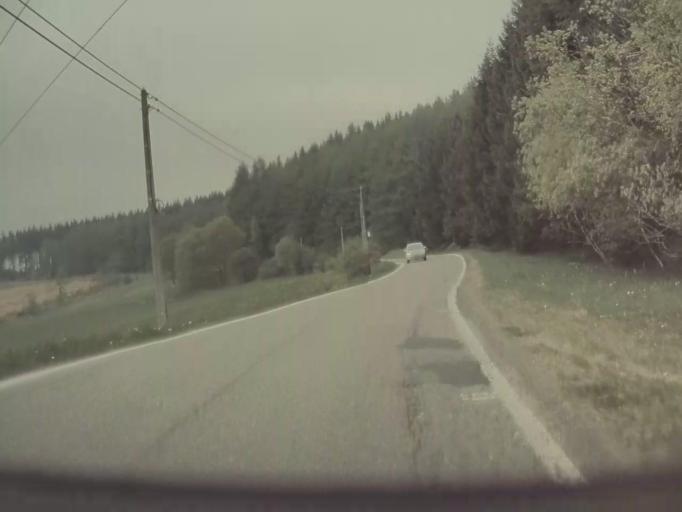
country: BE
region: Wallonia
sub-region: Province du Luxembourg
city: La Roche-en-Ardenne
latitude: 50.2271
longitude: 5.6241
